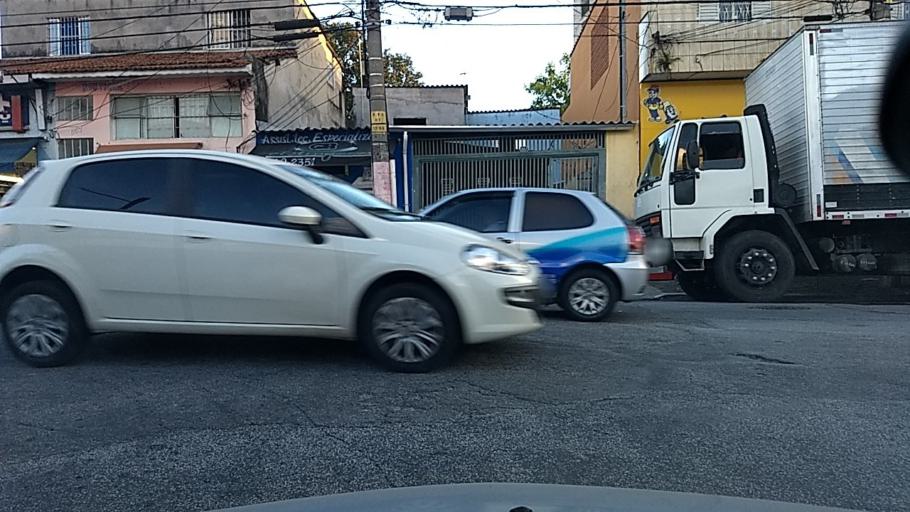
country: BR
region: Sao Paulo
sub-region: Guarulhos
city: Guarulhos
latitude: -23.4907
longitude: -46.5889
